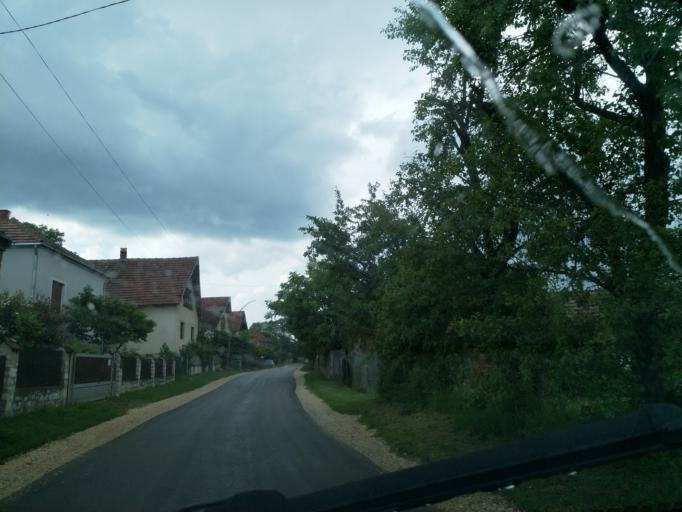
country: RS
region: Central Serbia
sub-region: Borski Okrug
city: Bor
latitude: 44.0136
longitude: 21.9838
